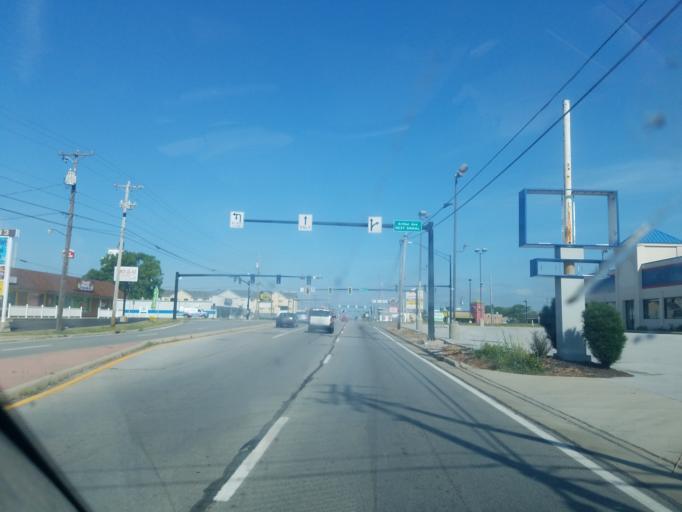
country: US
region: Ohio
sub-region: Allen County
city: Lima
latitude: 40.7603
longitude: -84.1438
